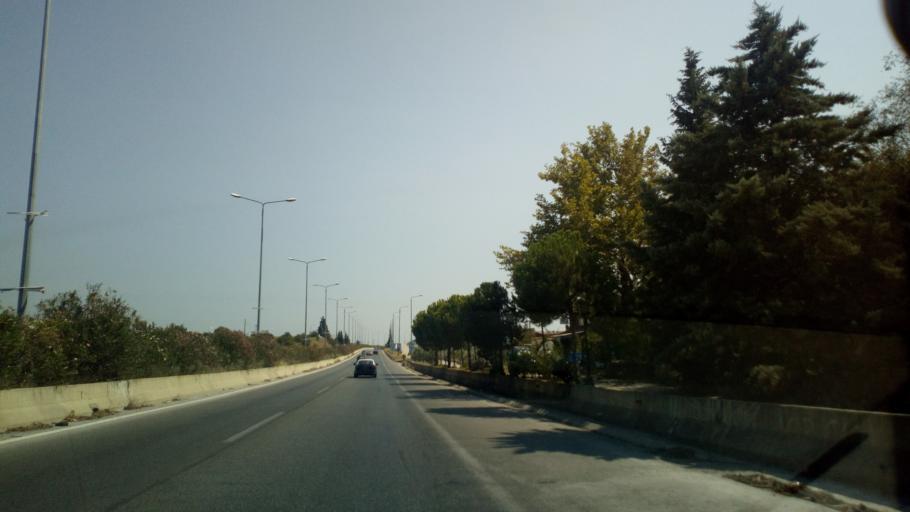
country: GR
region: Central Macedonia
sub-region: Nomos Thessalonikis
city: Mesimeri
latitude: 40.4106
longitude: 23.0248
